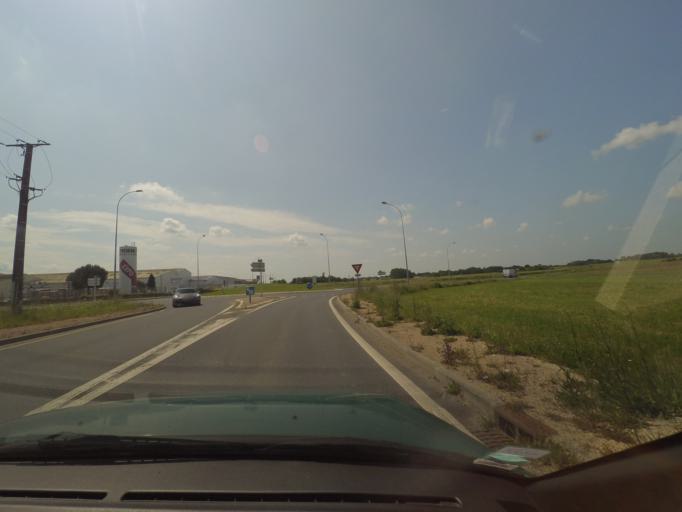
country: FR
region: Pays de la Loire
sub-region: Departement de la Loire-Atlantique
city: Mouzillon
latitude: 47.1260
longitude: -1.2826
